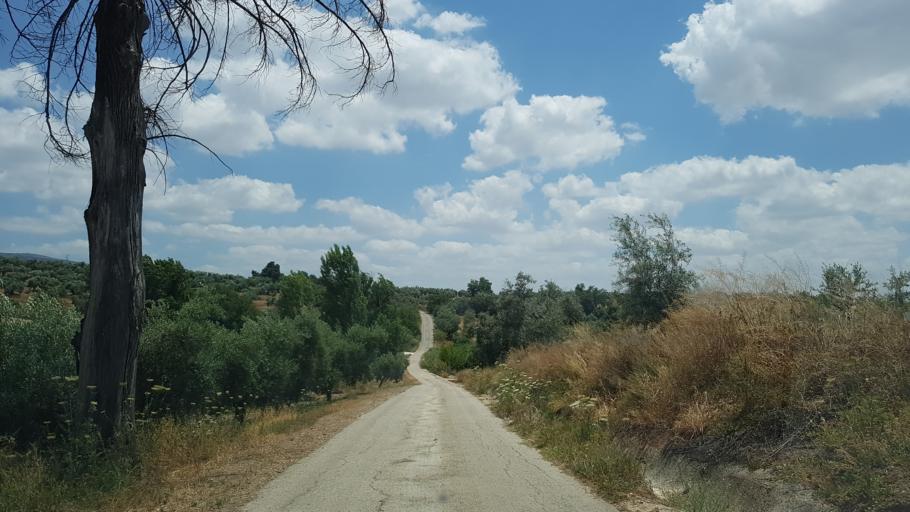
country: ES
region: Andalusia
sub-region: Province of Cordoba
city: Cabra
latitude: 37.5199
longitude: -4.4576
